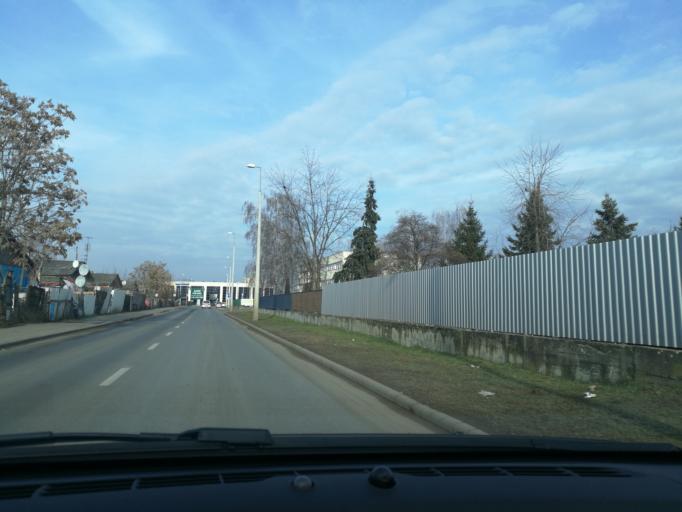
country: HU
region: Szabolcs-Szatmar-Bereg
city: Nyiregyhaza
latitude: 47.9503
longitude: 21.7402
